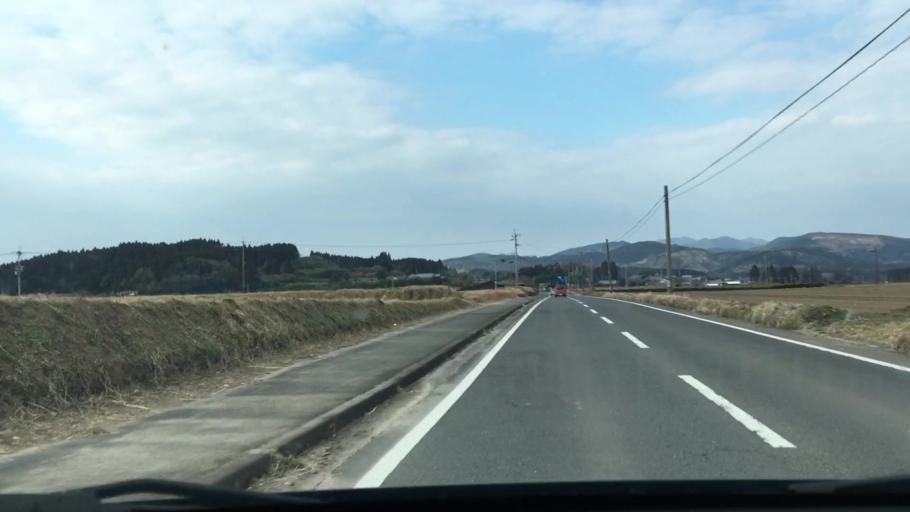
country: JP
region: Miyazaki
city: Kushima
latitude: 31.5159
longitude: 131.2395
